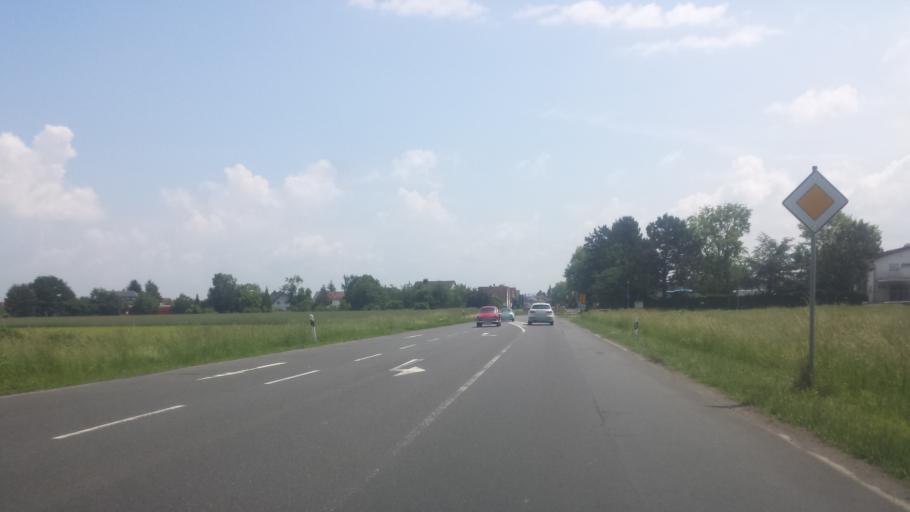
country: DE
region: Hesse
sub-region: Regierungsbezirk Darmstadt
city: Eppertshausen
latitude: 49.9517
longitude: 8.8349
